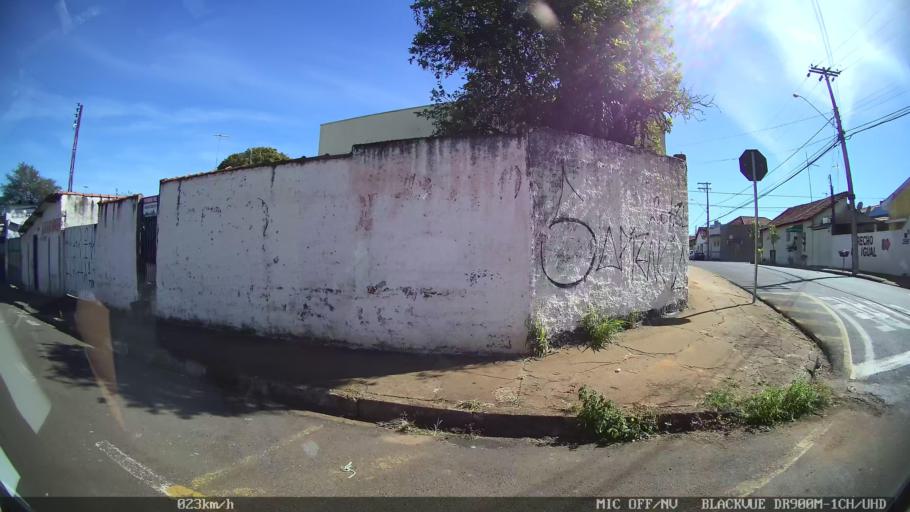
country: BR
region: Sao Paulo
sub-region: Franca
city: Franca
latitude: -20.5481
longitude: -47.3941
